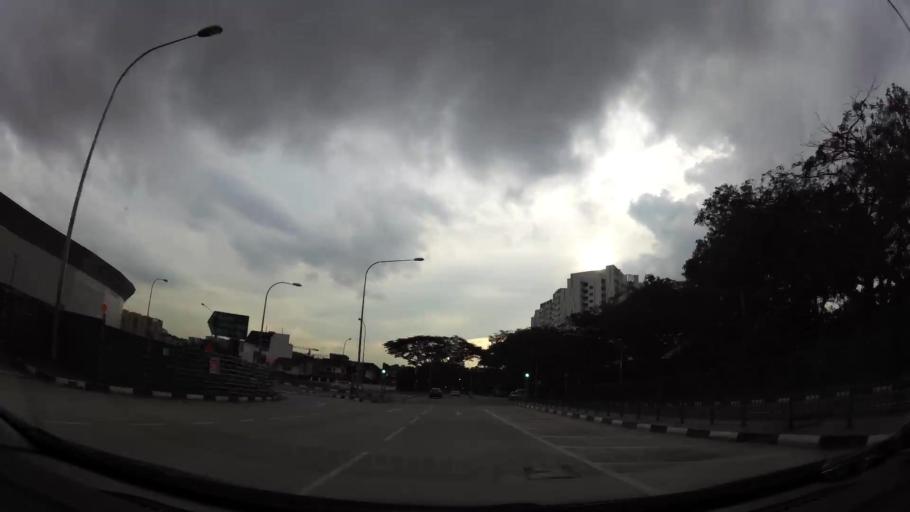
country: MY
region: Johor
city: Kampung Pasir Gudang Baru
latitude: 1.4519
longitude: 103.8298
